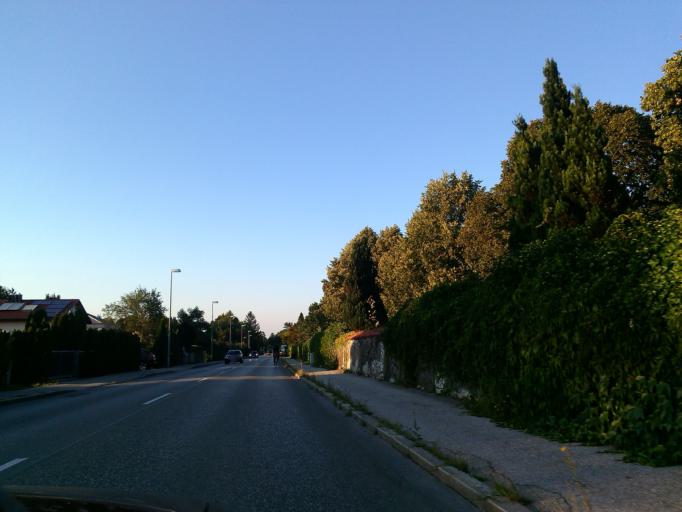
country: DE
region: Bavaria
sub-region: Upper Bavaria
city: Gauting
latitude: 48.0731
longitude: 11.3919
